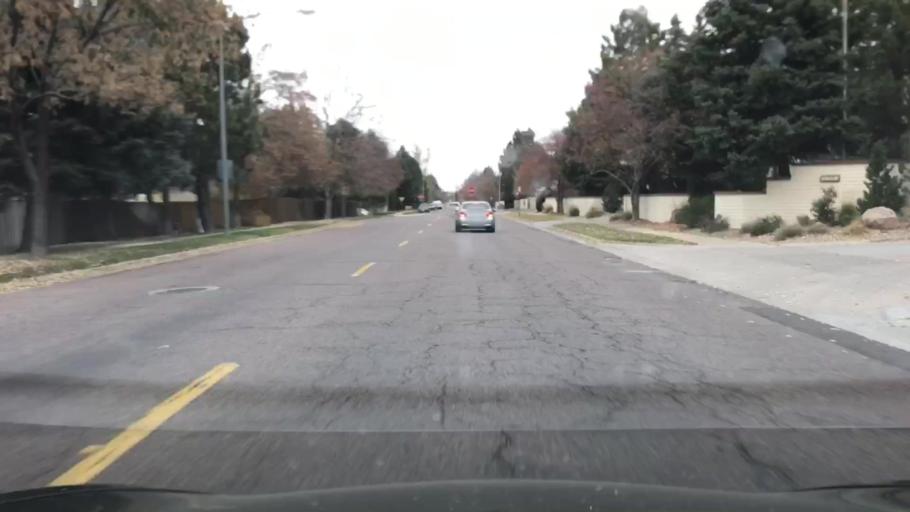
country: US
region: Colorado
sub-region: Arapahoe County
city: Glendale
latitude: 39.6885
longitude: -104.8959
